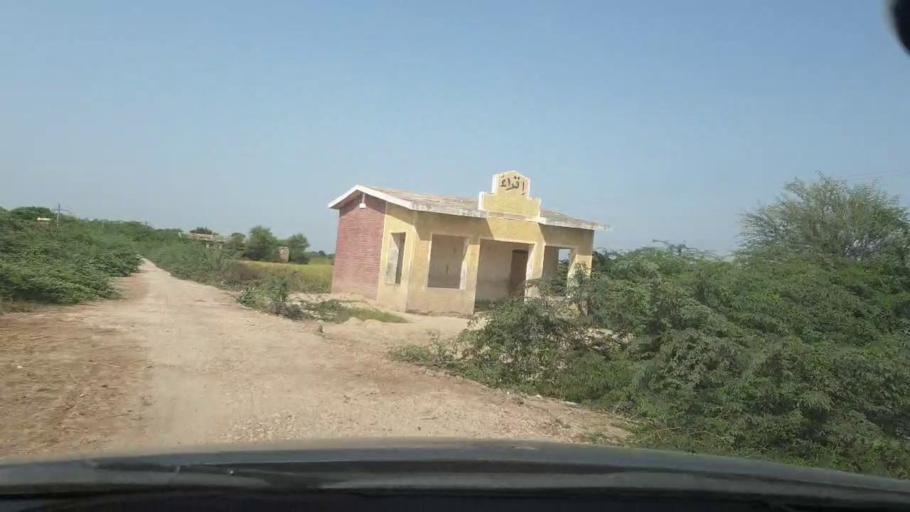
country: PK
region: Sindh
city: Naukot
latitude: 24.8016
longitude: 69.2579
